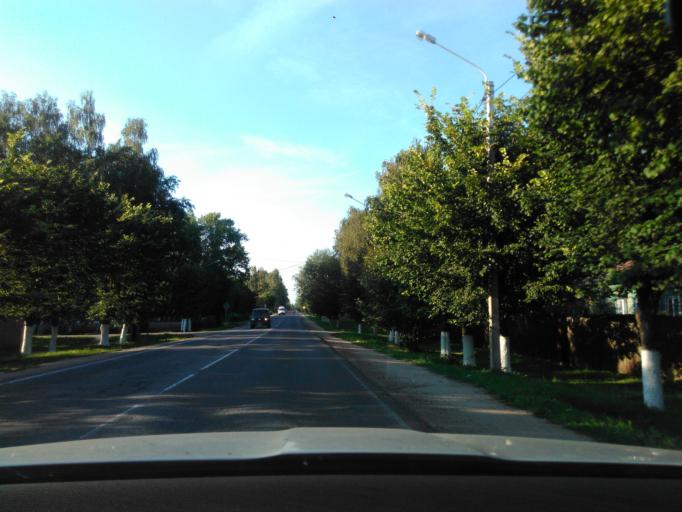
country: RU
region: Tverskaya
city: Konakovo
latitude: 56.6841
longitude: 36.7618
